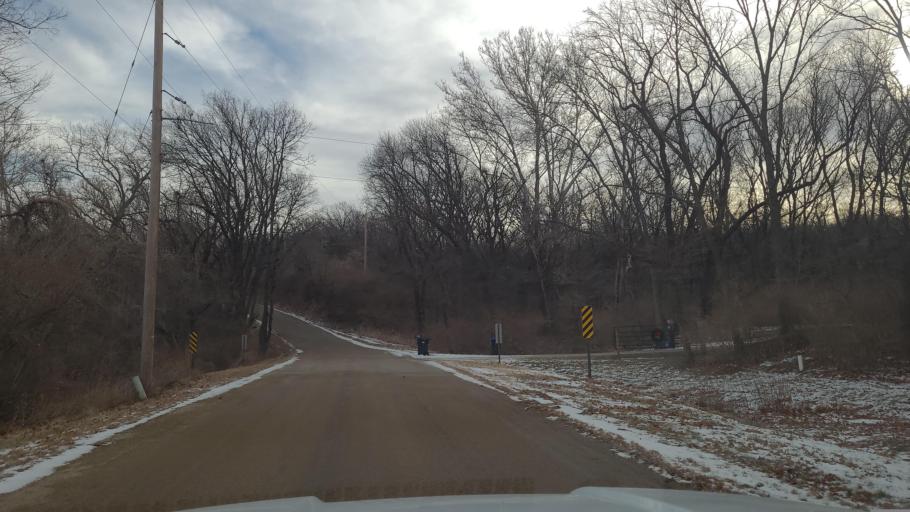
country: US
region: Kansas
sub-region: Shawnee County
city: Topeka
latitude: 39.0510
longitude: -95.5083
